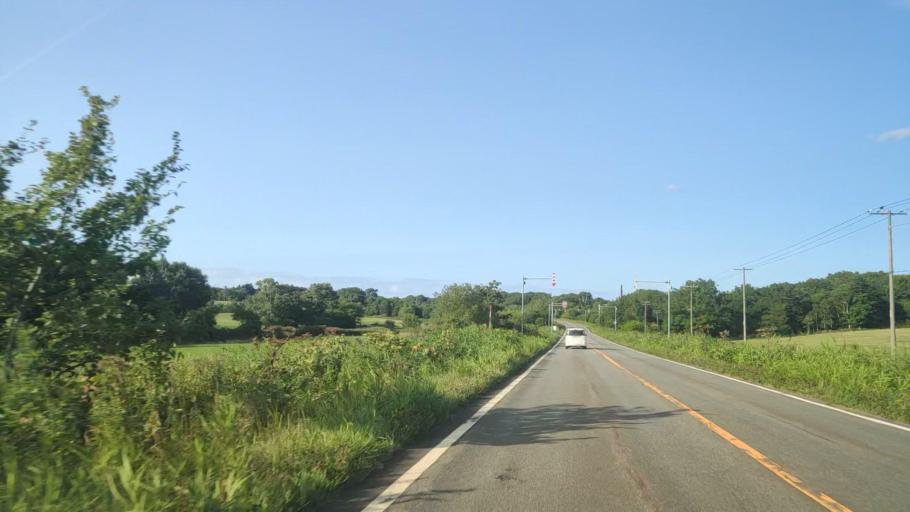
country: JP
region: Hokkaido
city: Makubetsu
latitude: 45.0712
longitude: 141.7510
